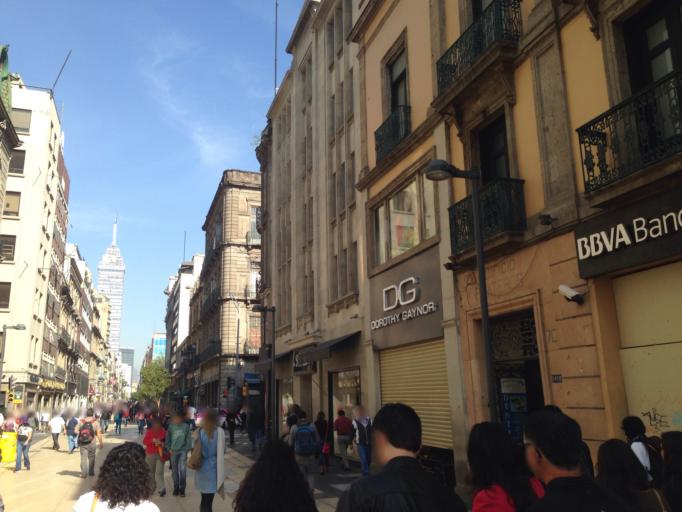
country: MX
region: Mexico City
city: Mexico City
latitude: 19.4332
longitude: -99.1349
